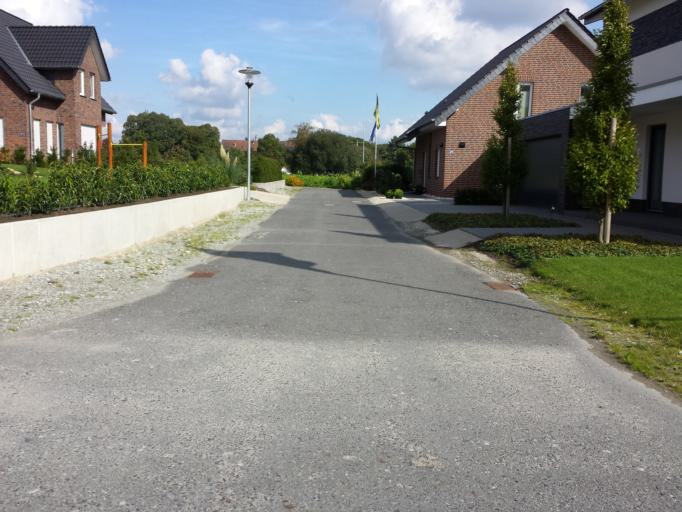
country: DE
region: North Rhine-Westphalia
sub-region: Regierungsbezirk Detmold
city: Langenberg
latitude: 51.7842
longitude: 8.3158
